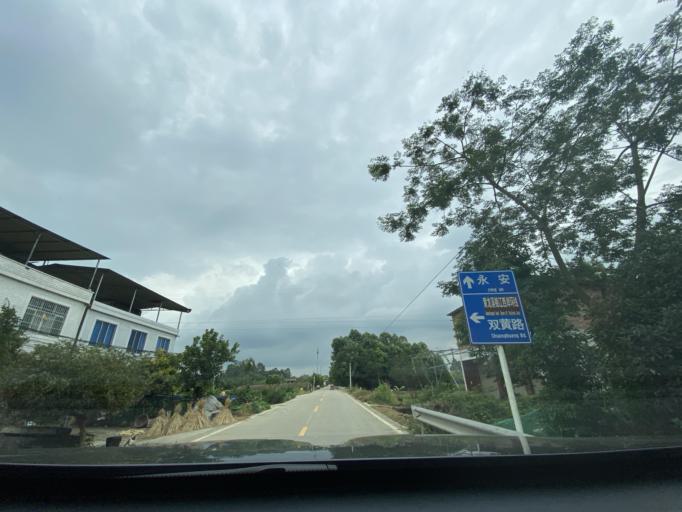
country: CN
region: Sichuan
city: Wujin
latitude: 30.3828
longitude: 103.9677
